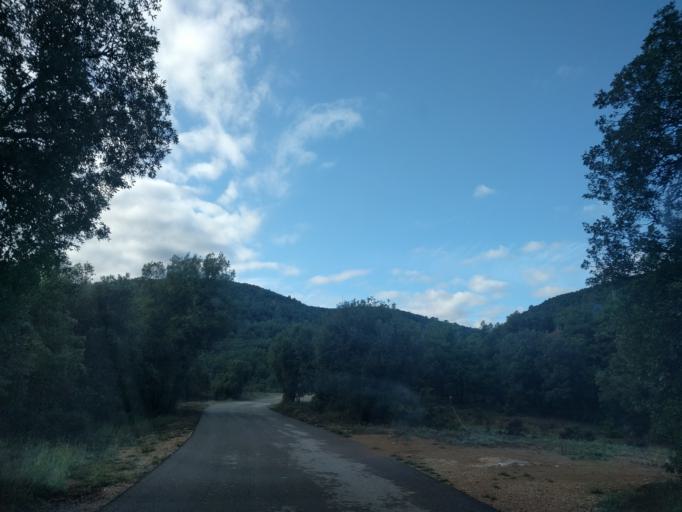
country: ES
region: Catalonia
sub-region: Provincia de Girona
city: Sant Aniol de Finestres
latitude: 42.0522
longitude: 2.6255
